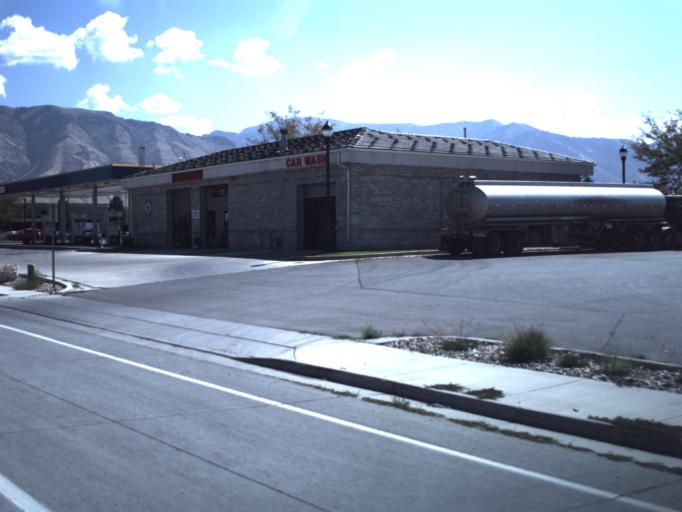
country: US
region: Utah
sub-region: Cache County
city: Hyde Park
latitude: 41.7777
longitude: -111.8354
